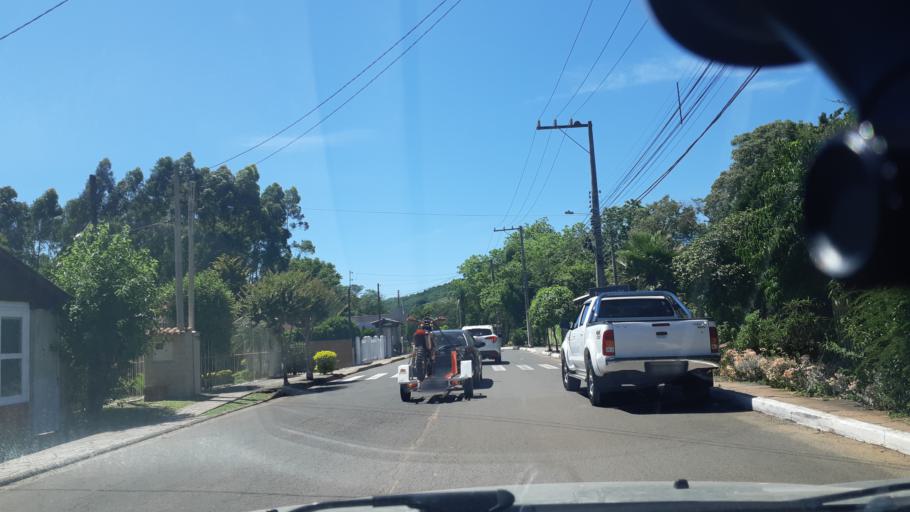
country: BR
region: Rio Grande do Sul
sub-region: Ivoti
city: Ivoti
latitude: -29.6189
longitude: -51.1217
